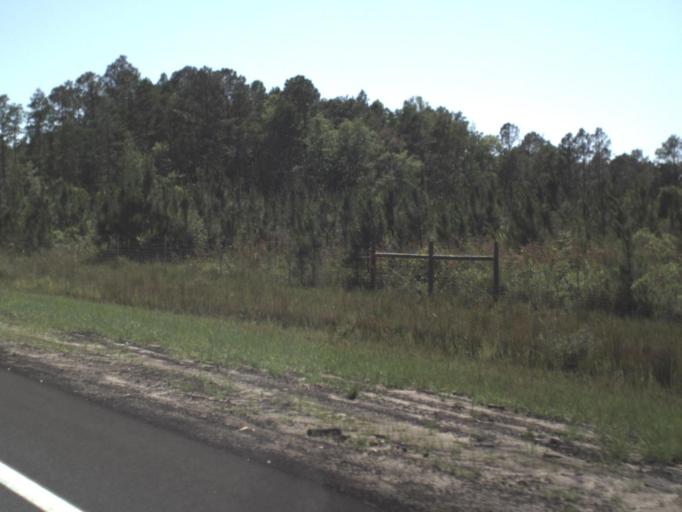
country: US
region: Florida
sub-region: Duval County
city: Baldwin
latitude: 30.3618
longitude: -81.9476
